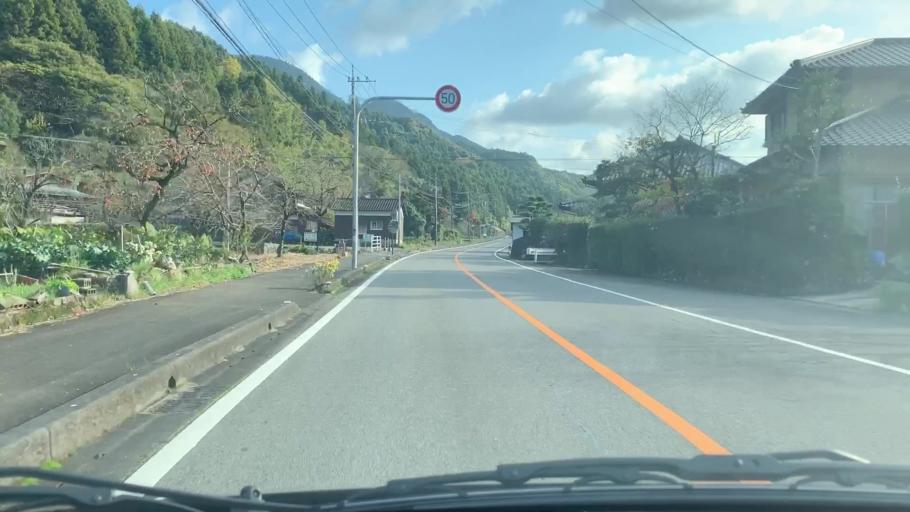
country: JP
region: Saga Prefecture
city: Kashima
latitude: 33.0723
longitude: 130.0688
